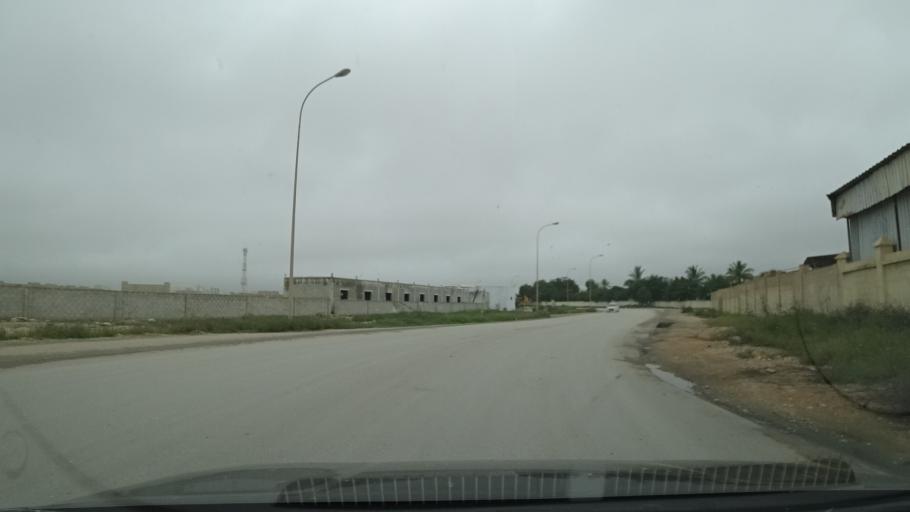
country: OM
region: Zufar
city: Salalah
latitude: 17.0119
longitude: 54.0443
